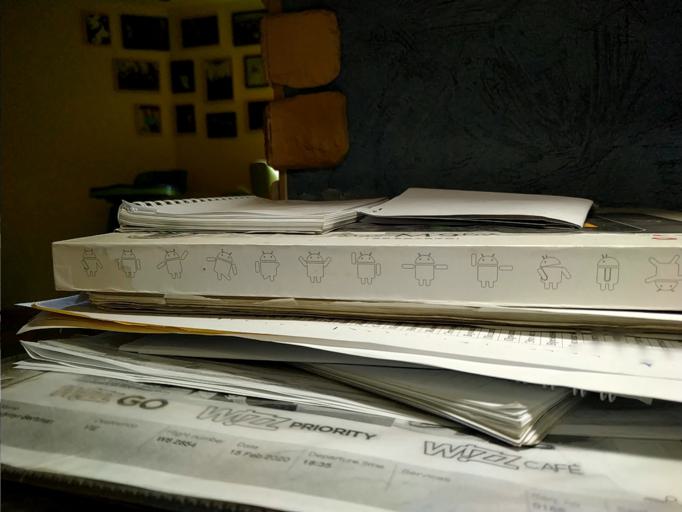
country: RU
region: Novgorod
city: Sol'tsy
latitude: 58.0855
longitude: 30.1309
